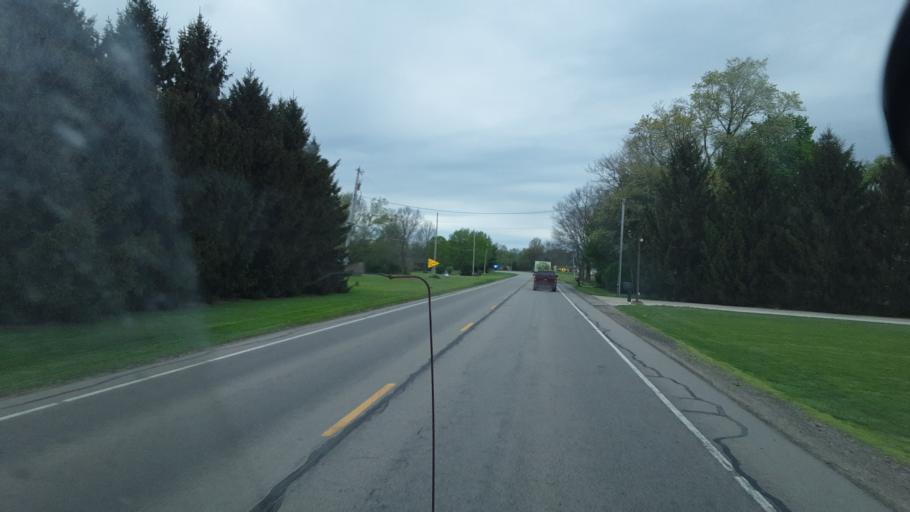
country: US
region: Indiana
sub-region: Elkhart County
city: New Paris
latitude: 41.5138
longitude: -85.7656
